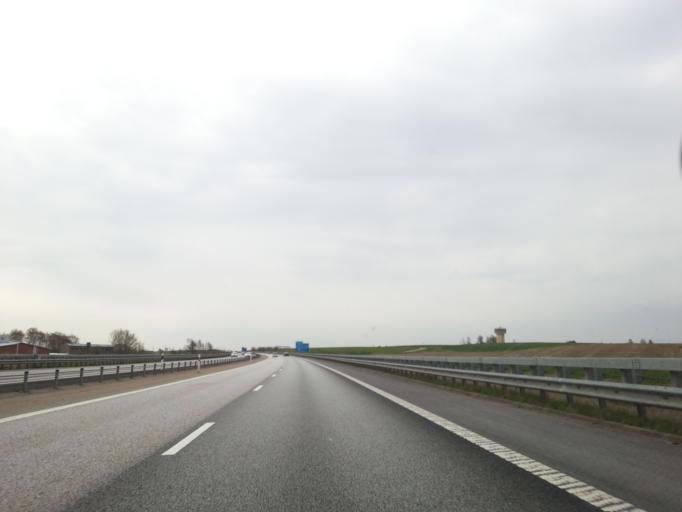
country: SE
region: Skane
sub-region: Angelholms Kommun
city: AEngelholm
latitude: 56.2678
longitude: 12.8931
